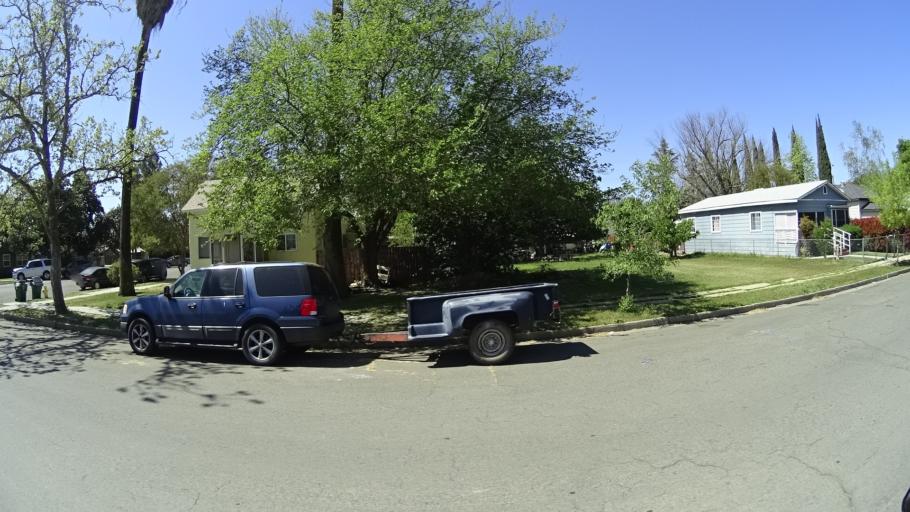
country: US
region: California
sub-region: Glenn County
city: Willows
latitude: 39.5220
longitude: -122.1968
